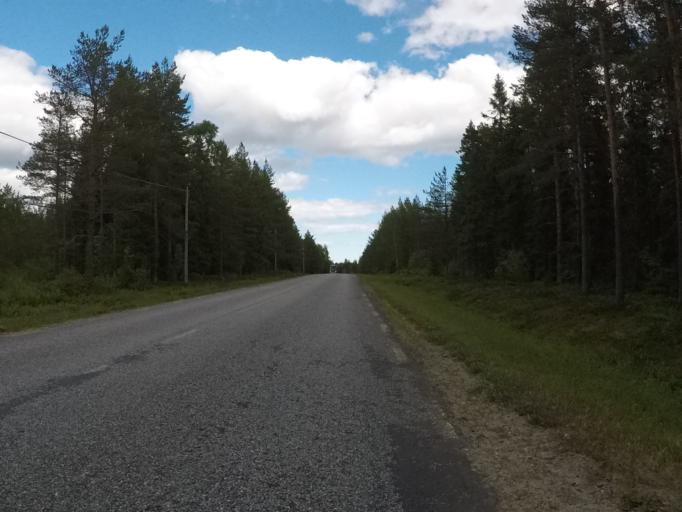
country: SE
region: Vaesterbotten
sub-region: Umea Kommun
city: Saevar
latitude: 63.9262
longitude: 20.7743
